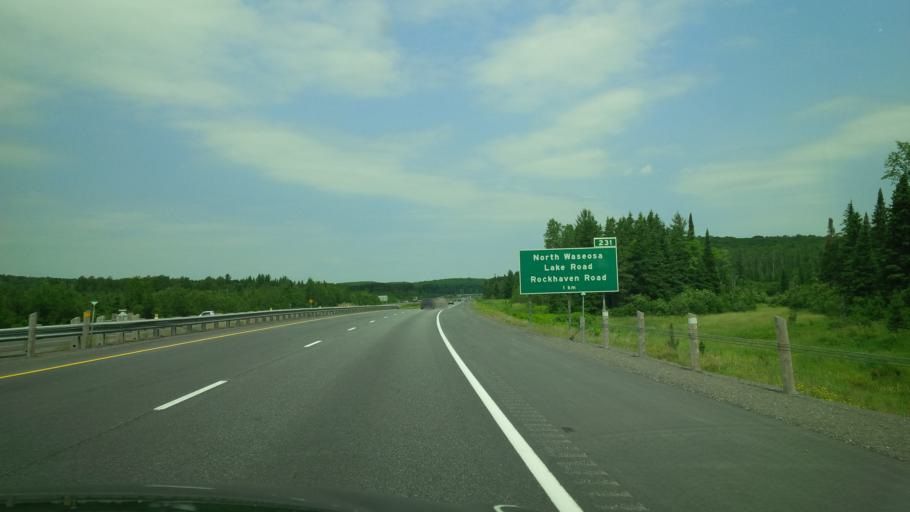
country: CA
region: Ontario
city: Huntsville
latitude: 45.3962
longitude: -79.2373
